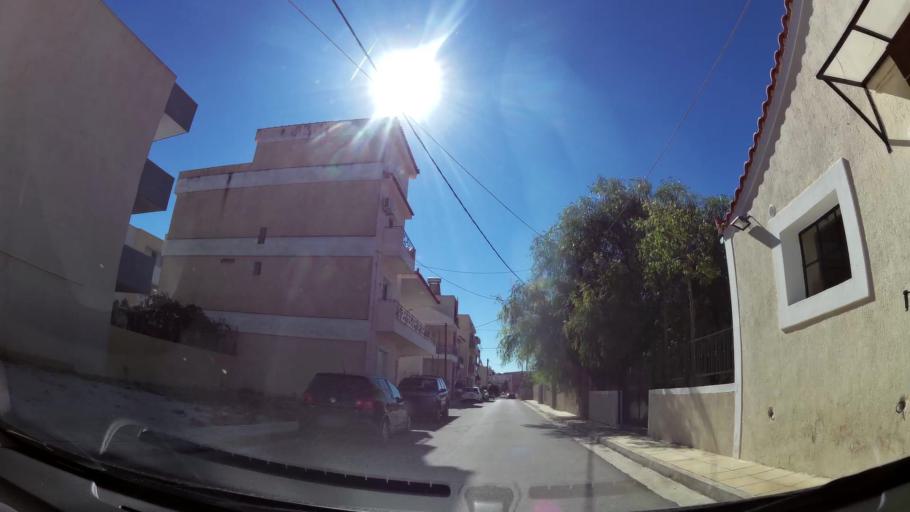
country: GR
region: Attica
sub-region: Nomarchia Anatolikis Attikis
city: Koropi
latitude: 37.9104
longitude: 23.8763
